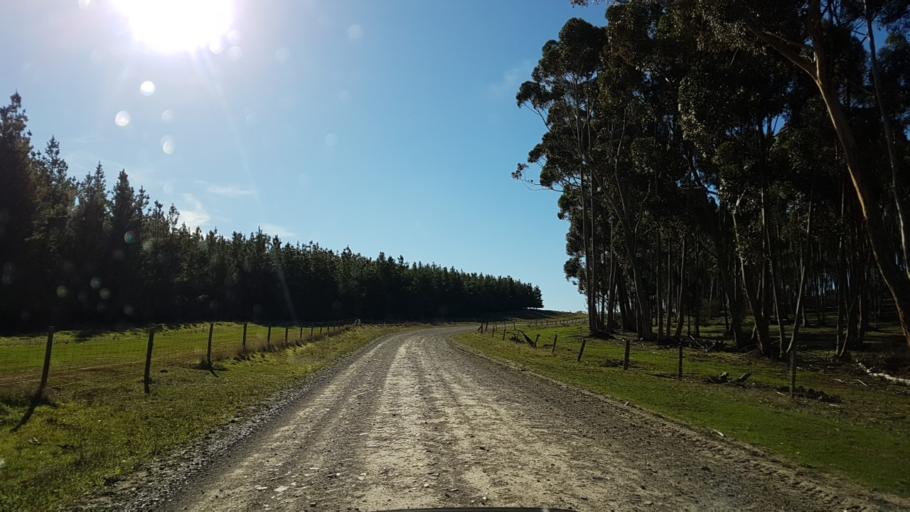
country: AU
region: South Australia
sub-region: Northern Areas
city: Jamestown
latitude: -33.2842
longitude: 138.5597
